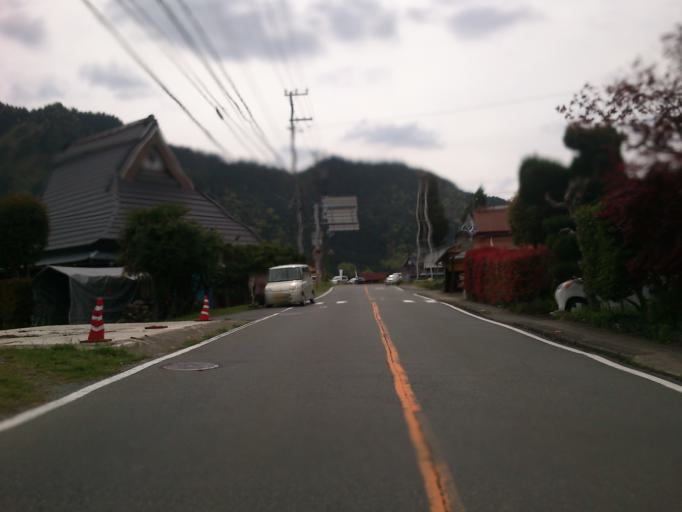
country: JP
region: Kyoto
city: Maizuru
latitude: 35.2750
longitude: 135.5467
